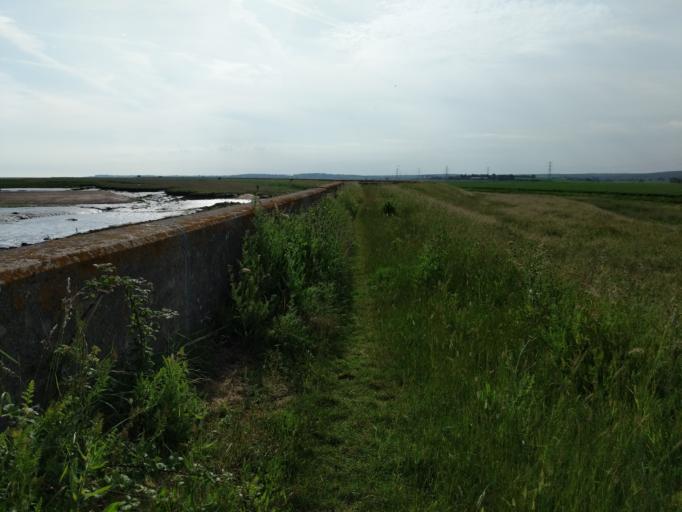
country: GB
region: England
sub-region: Kent
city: Faversham
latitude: 51.3436
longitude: 0.9131
